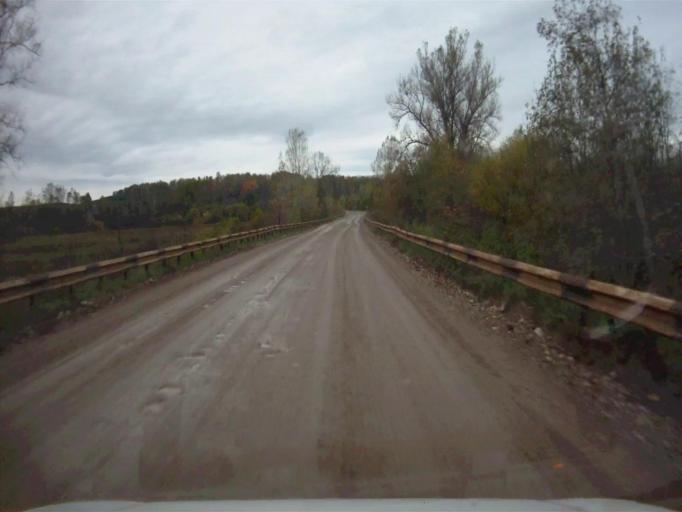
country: RU
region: Chelyabinsk
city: Nyazepetrovsk
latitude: 56.1320
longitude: 59.3199
